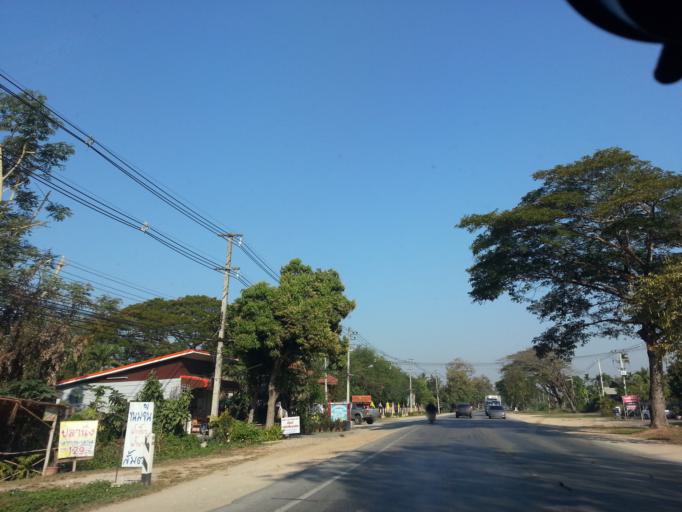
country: TH
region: Chiang Mai
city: San Sai
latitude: 18.9284
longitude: 98.9908
